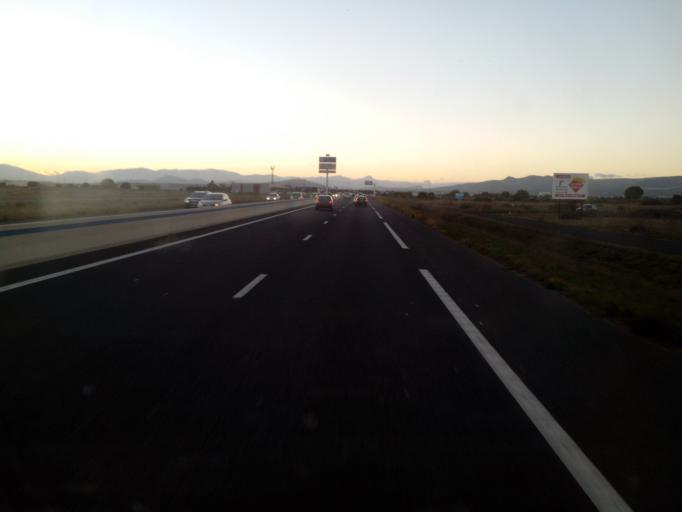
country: FR
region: Languedoc-Roussillon
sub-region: Departement des Pyrenees-Orientales
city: Claira
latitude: 42.7775
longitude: 2.9284
